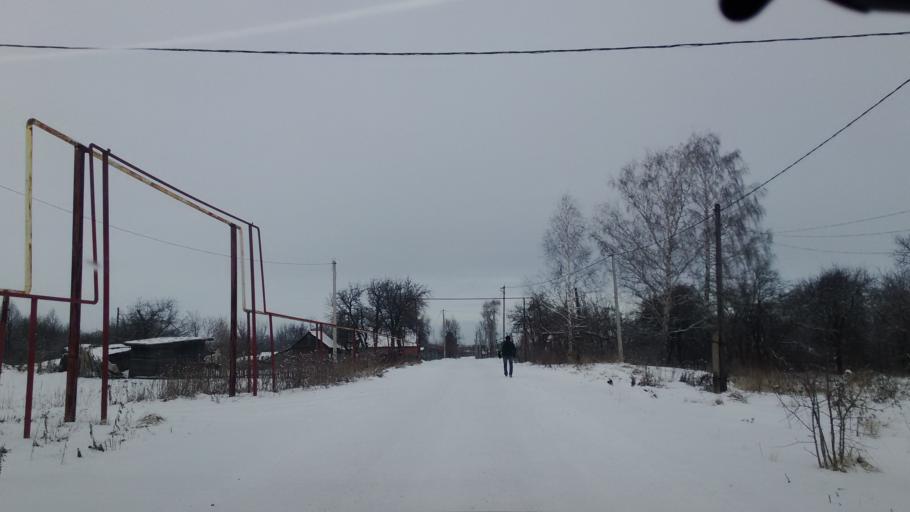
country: RU
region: Tula
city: Bogoroditsk
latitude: 53.7525
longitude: 38.1062
